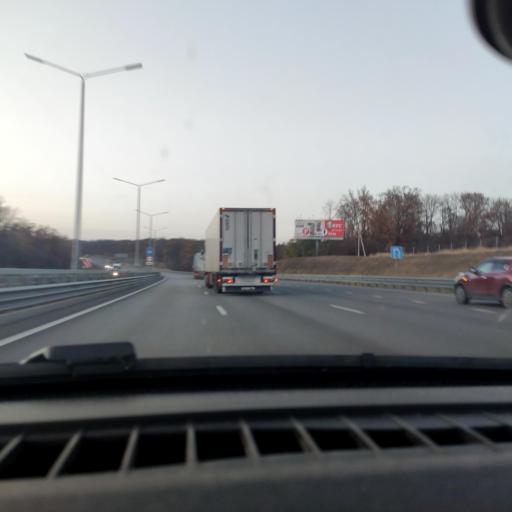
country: RU
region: Voronezj
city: Ramon'
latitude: 51.8258
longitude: 39.2485
